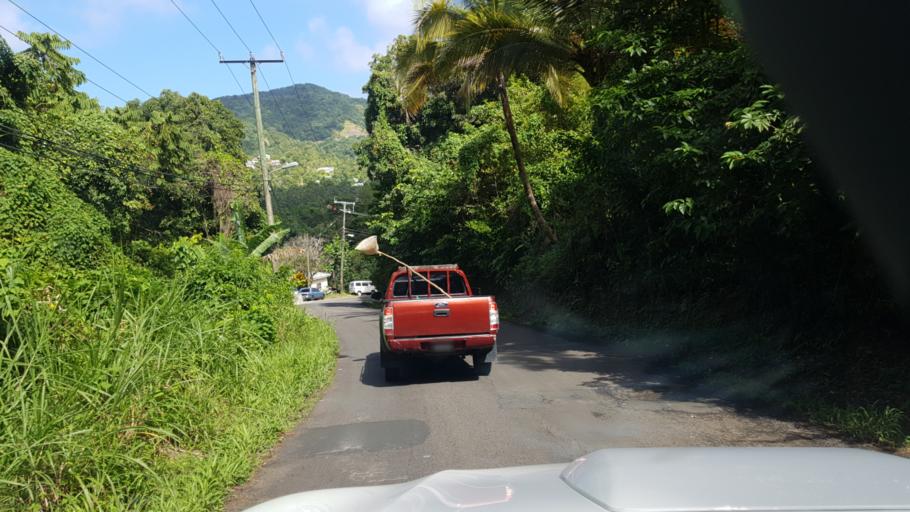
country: LC
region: Castries Quarter
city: Bisee
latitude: 14.0139
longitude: -60.9621
